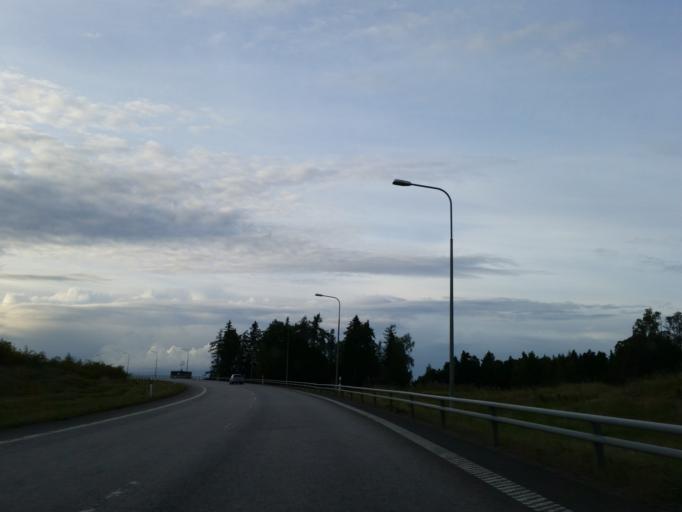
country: SE
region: Uppsala
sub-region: Uppsala Kommun
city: Saevja
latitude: 59.8345
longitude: 17.7350
